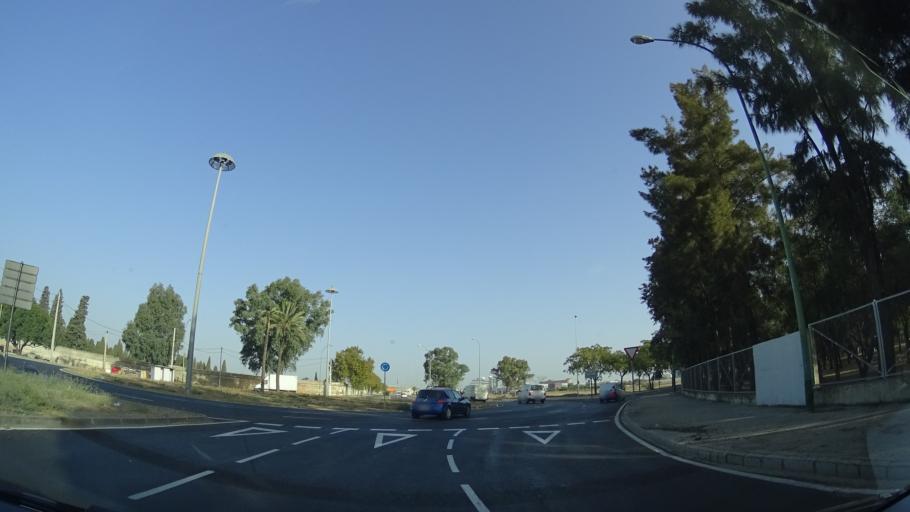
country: ES
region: Andalusia
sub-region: Provincia de Sevilla
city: Sevilla
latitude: 37.4202
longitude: -5.9765
